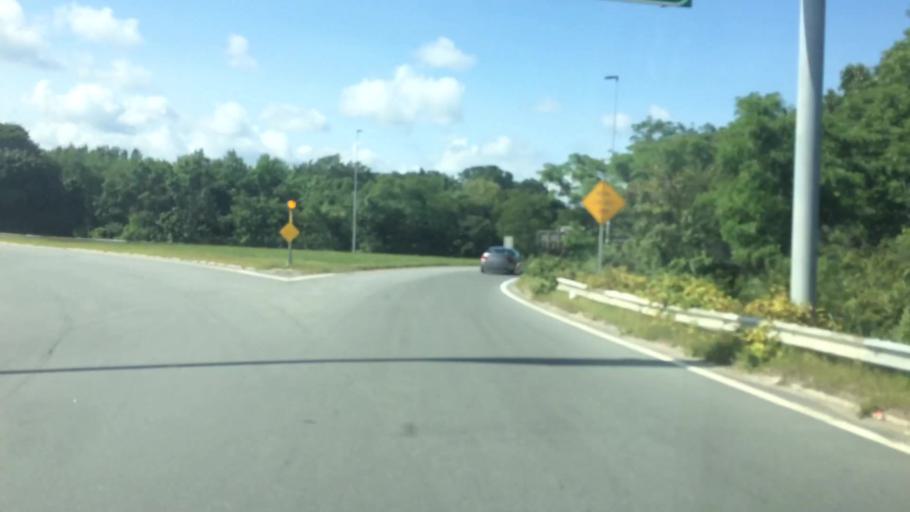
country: US
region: Massachusetts
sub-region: Essex County
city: South Peabody
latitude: 42.5133
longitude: -70.9906
